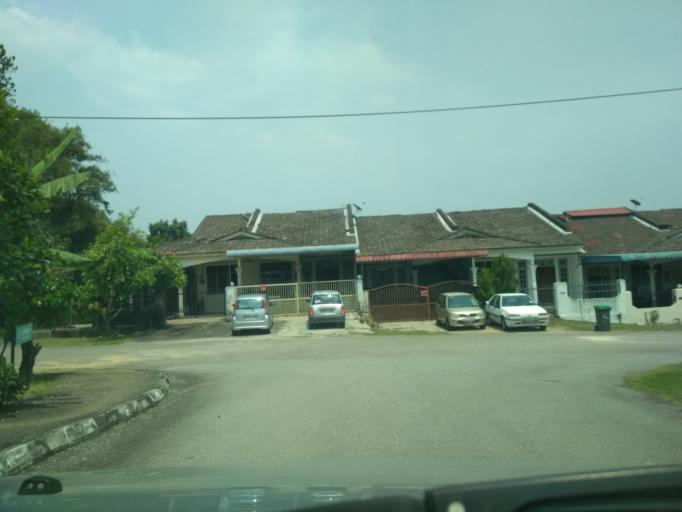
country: MY
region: Kedah
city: Kulim
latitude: 5.3570
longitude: 100.5330
